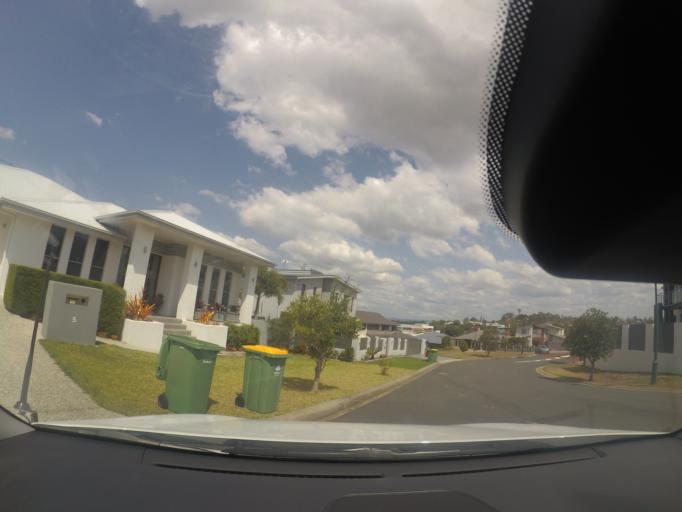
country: AU
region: Queensland
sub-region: Logan
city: Rochedale South
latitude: -27.6029
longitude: 153.1076
